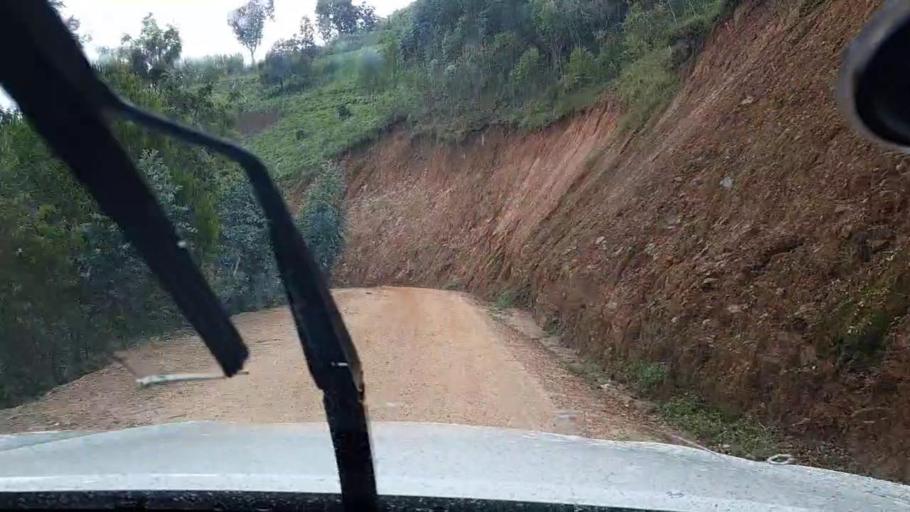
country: RW
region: Western Province
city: Kibuye
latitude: -2.1542
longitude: 29.4298
